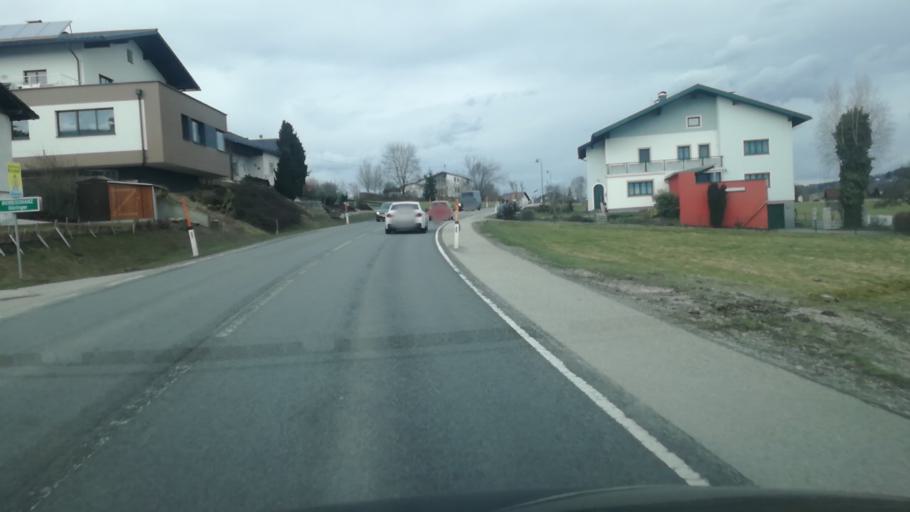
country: AT
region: Upper Austria
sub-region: Politischer Bezirk Vocklabruck
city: Frankenburg
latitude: 48.0596
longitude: 13.4804
